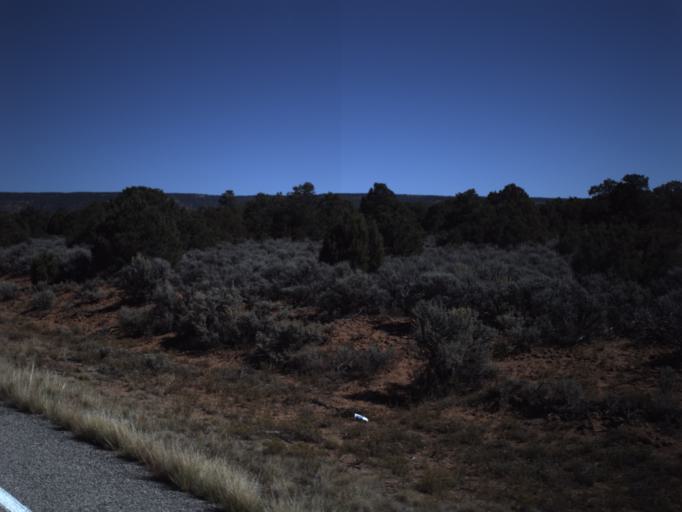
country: US
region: Utah
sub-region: San Juan County
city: Blanding
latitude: 37.5643
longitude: -109.9284
